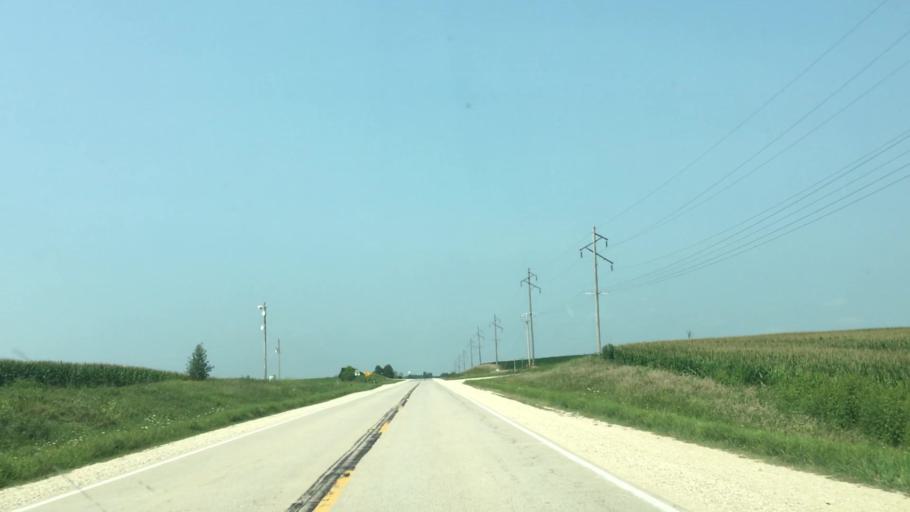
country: US
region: Iowa
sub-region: Winneshiek County
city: Decorah
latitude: 43.1460
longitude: -91.8643
